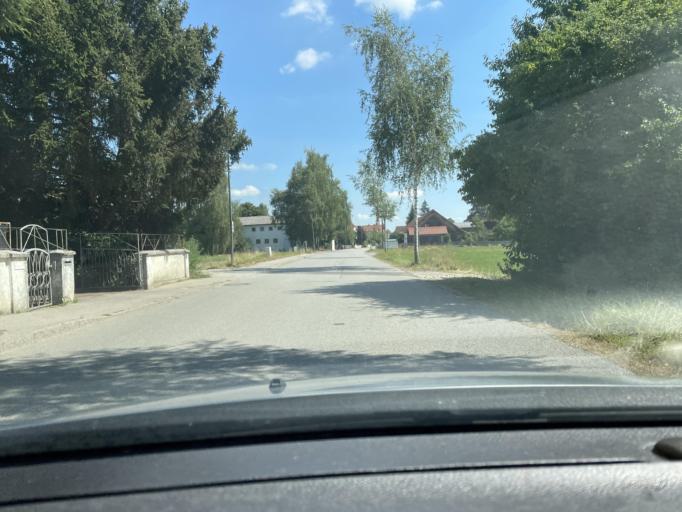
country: FR
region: Champagne-Ardenne
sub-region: Departement de la Marne
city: Pontfaverger-Moronvilliers
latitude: 49.2887
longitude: 4.3441
